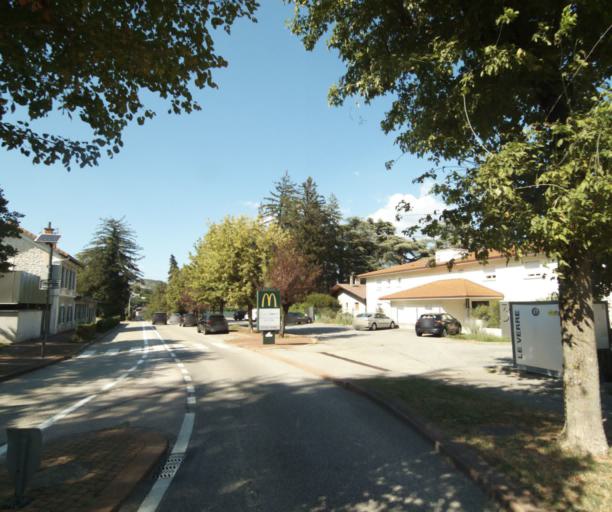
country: FR
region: Rhone-Alpes
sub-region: Departement de l'Isere
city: Seyssins
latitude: 45.1579
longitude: 5.6822
